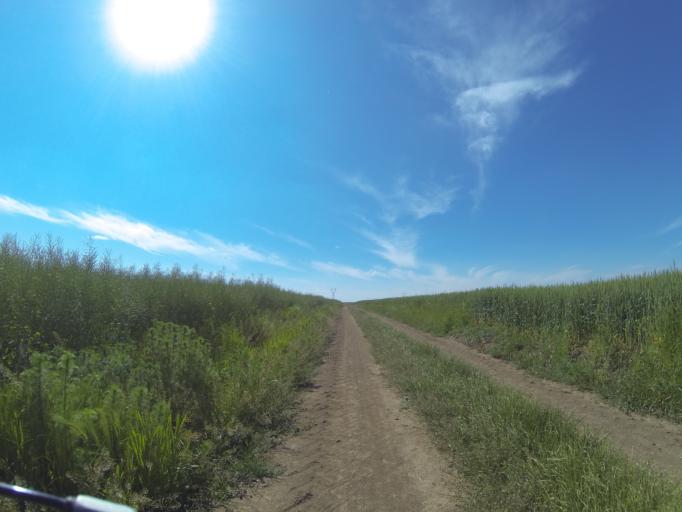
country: RO
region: Dolj
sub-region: Comuna Leu
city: Leu
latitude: 44.2563
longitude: 24.0083
